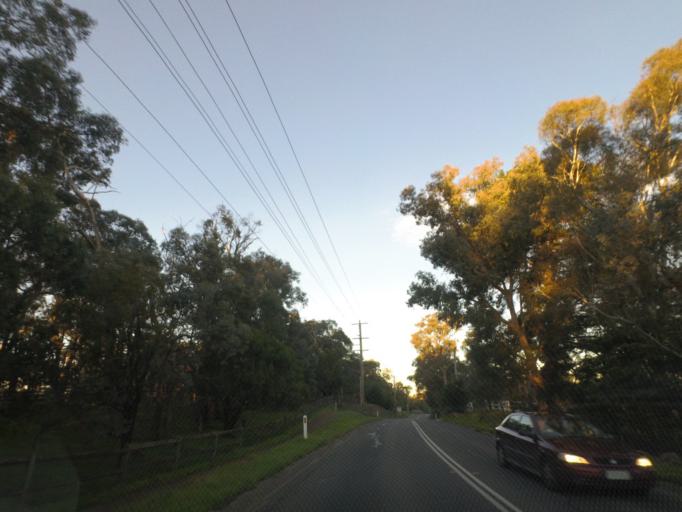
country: AU
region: Victoria
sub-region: Manningham
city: Warrandyte
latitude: -37.7338
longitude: 145.2623
